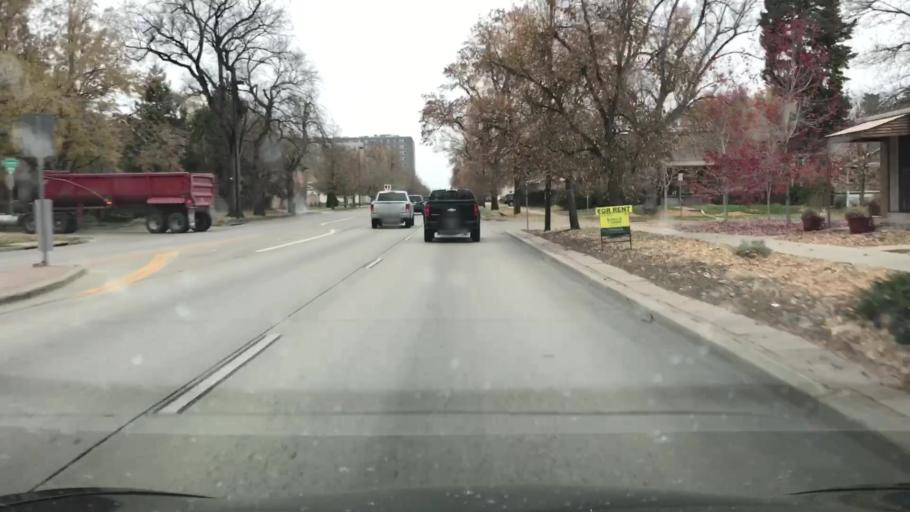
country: US
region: Colorado
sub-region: Arapahoe County
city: Glendale
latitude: 39.6785
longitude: -104.9532
